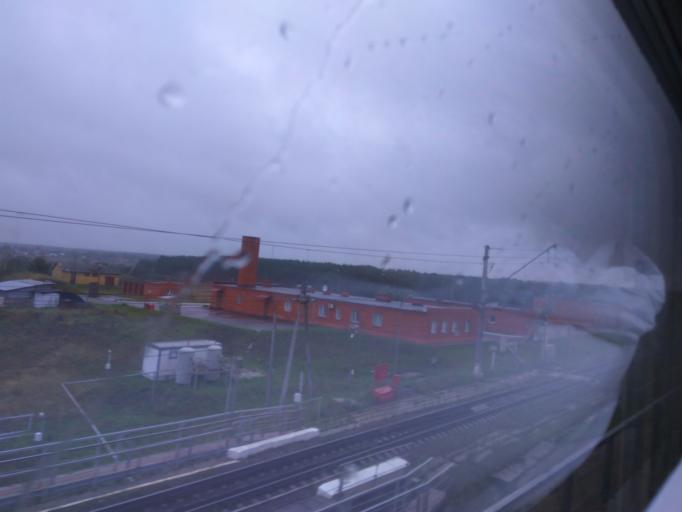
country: RU
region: Moskovskaya
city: Kashira
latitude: 54.8632
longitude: 38.1625
